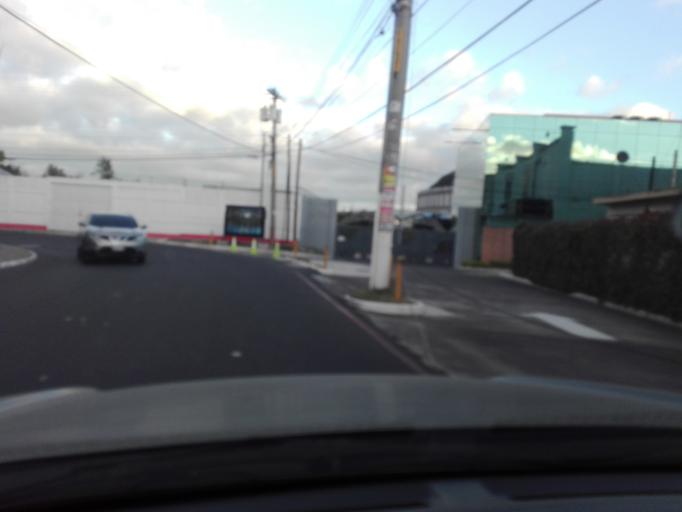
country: GT
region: Guatemala
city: Mixco
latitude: 14.5940
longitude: -90.5775
